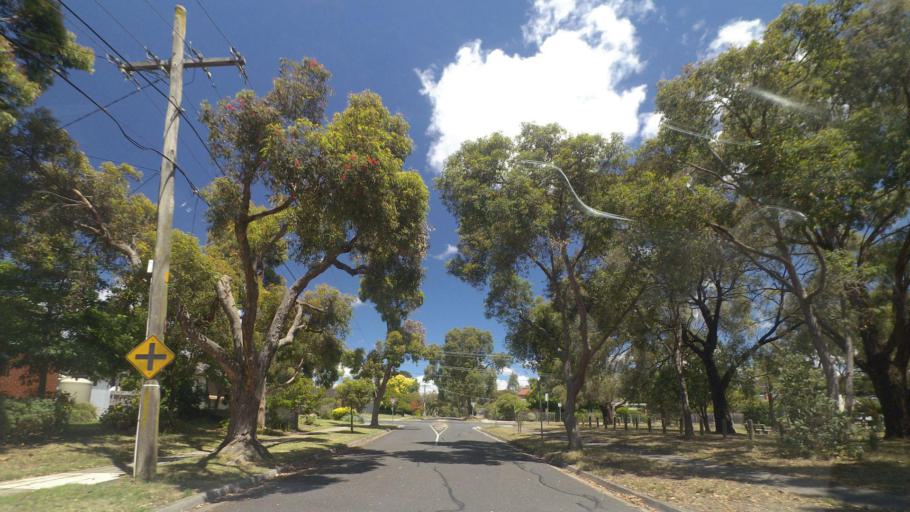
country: AU
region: Victoria
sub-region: Maroondah
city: Croydon South
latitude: -37.8155
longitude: 145.2831
